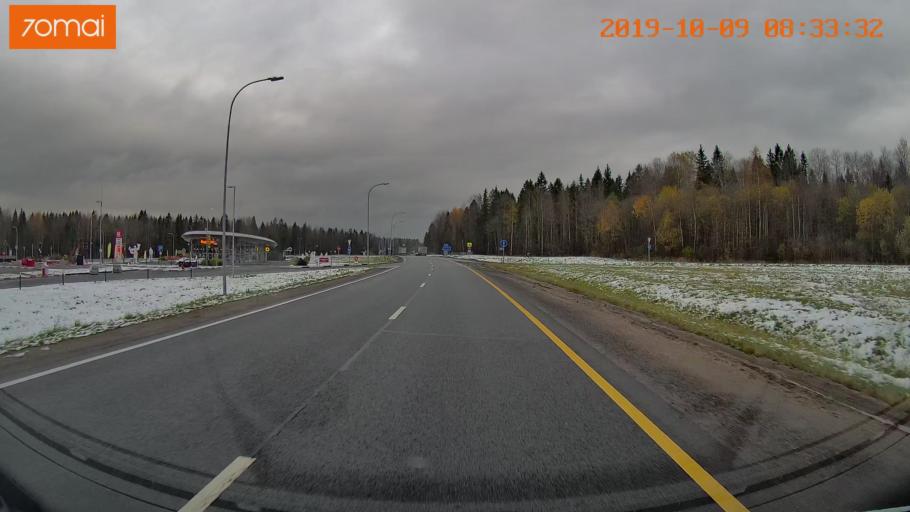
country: RU
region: Vologda
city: Gryazovets
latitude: 58.8834
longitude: 40.1926
